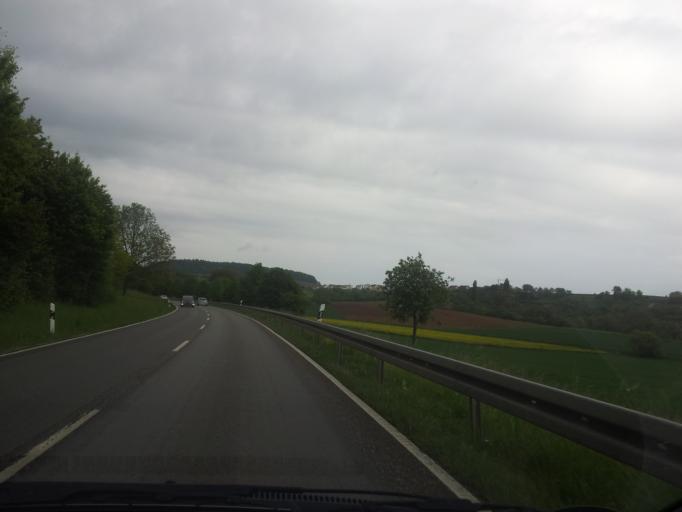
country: DE
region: Baden-Wuerttemberg
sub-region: Regierungsbezirk Stuttgart
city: Abstatt
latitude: 49.0498
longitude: 9.2896
